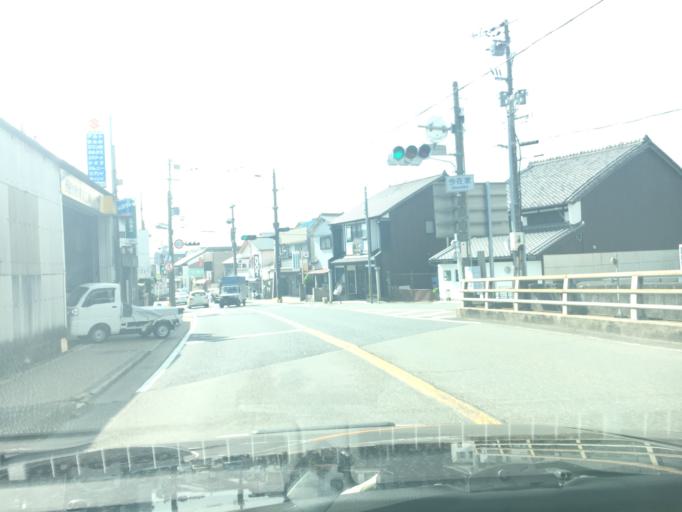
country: JP
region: Nara
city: Nara-shi
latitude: 34.6946
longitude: 135.8353
